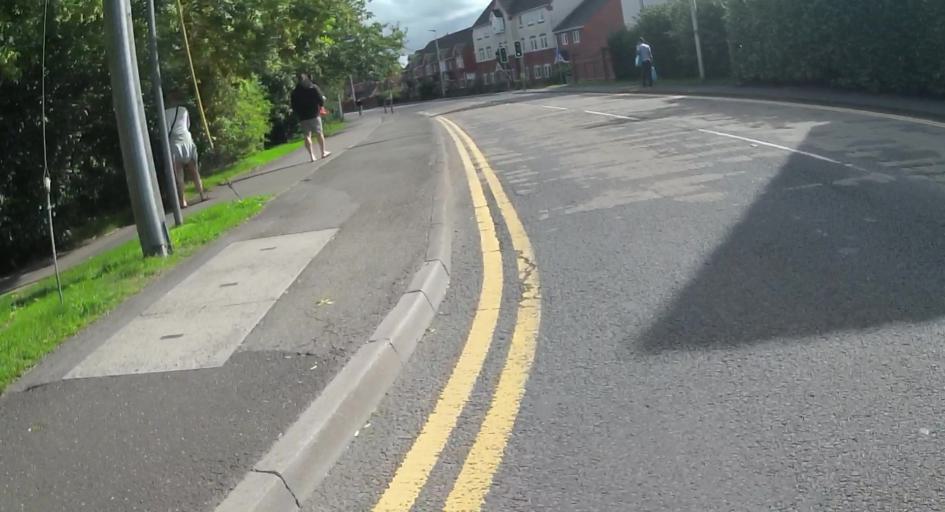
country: GB
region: England
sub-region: West Berkshire
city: Thatcham
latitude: 51.3970
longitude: -1.2486
